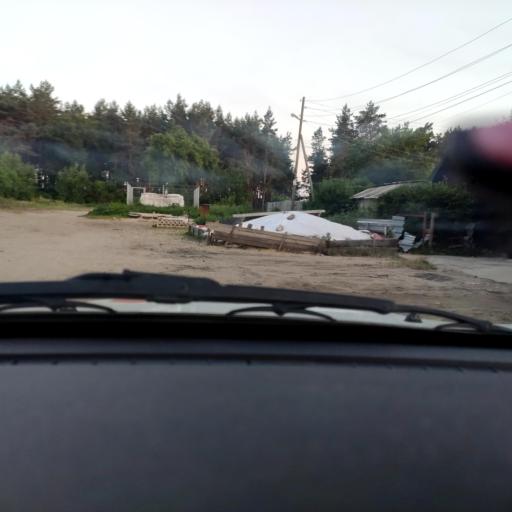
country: RU
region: Voronezj
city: Maslovka
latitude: 51.6056
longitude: 39.2246
